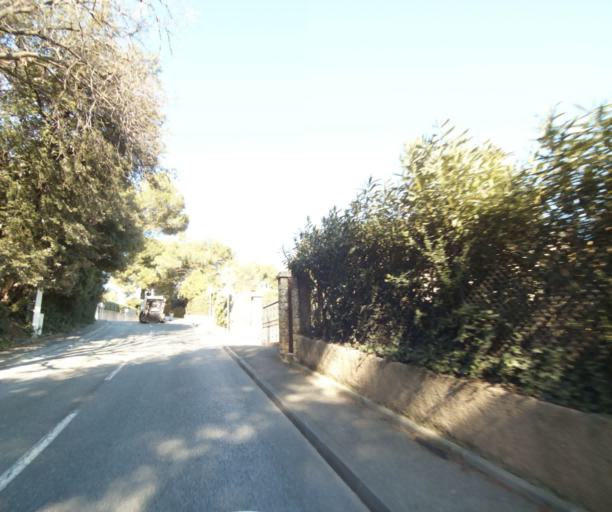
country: FR
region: Provence-Alpes-Cote d'Azur
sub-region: Departement des Alpes-Maritimes
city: Biot
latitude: 43.6057
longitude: 7.0900
